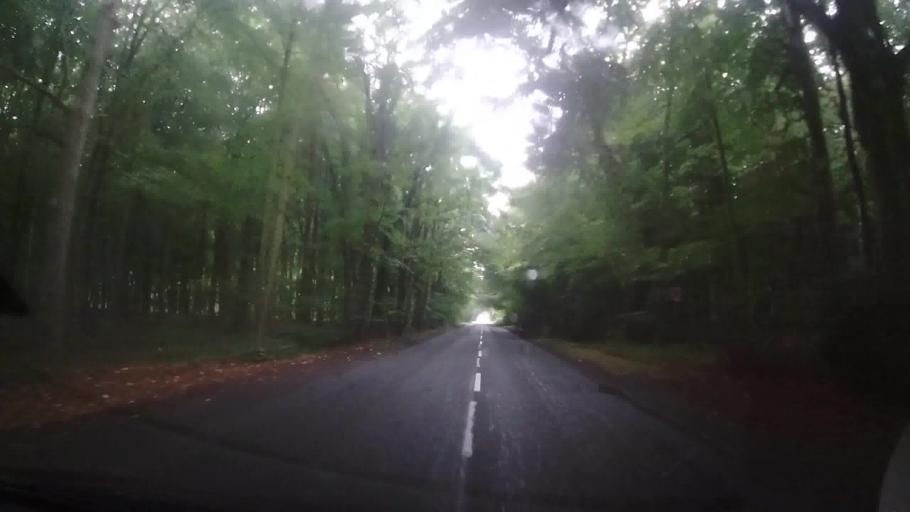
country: GB
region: England
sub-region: Oxfordshire
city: Stonesfield
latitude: 51.8712
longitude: -1.4258
